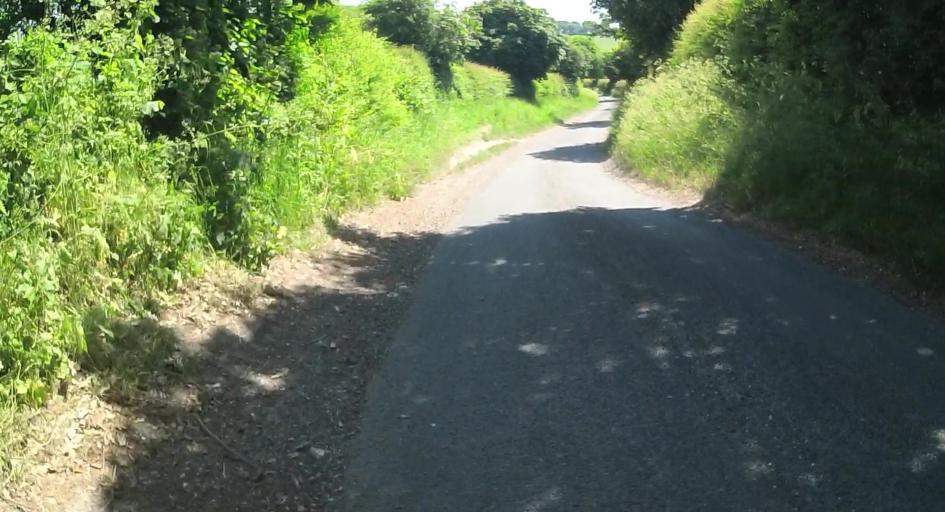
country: GB
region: England
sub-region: Hampshire
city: Kingsclere
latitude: 51.3158
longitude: -1.2952
